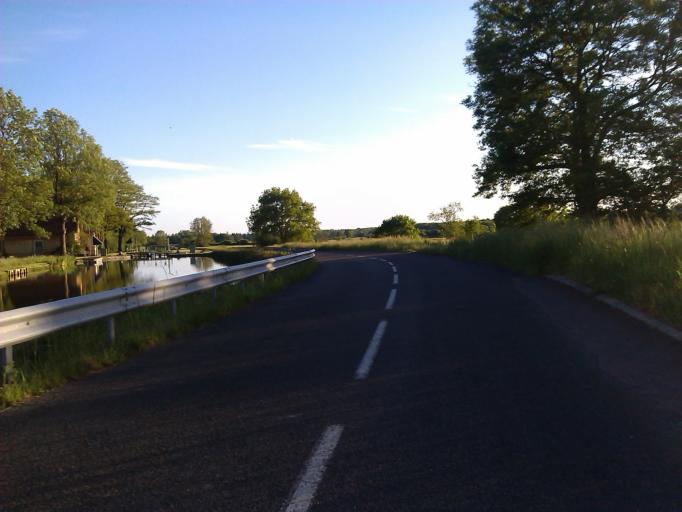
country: FR
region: Bourgogne
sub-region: Departement de Saone-et-Loire
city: Palinges
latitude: 46.5430
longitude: 4.2097
